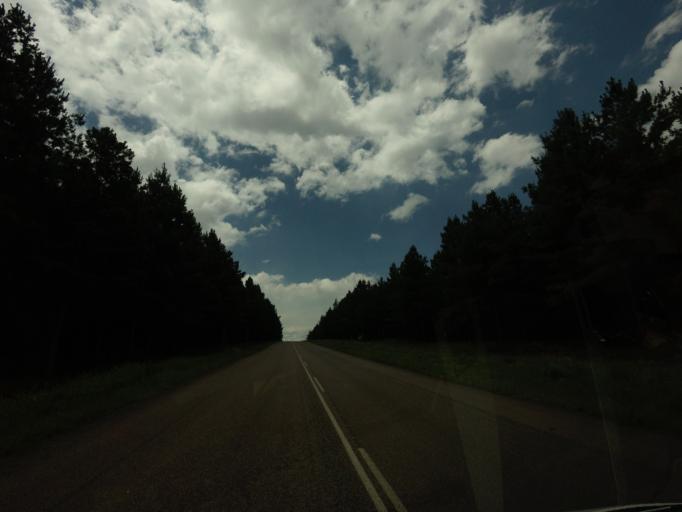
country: ZA
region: Mpumalanga
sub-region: Ehlanzeni District
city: Graksop
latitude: -25.0281
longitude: 30.8214
